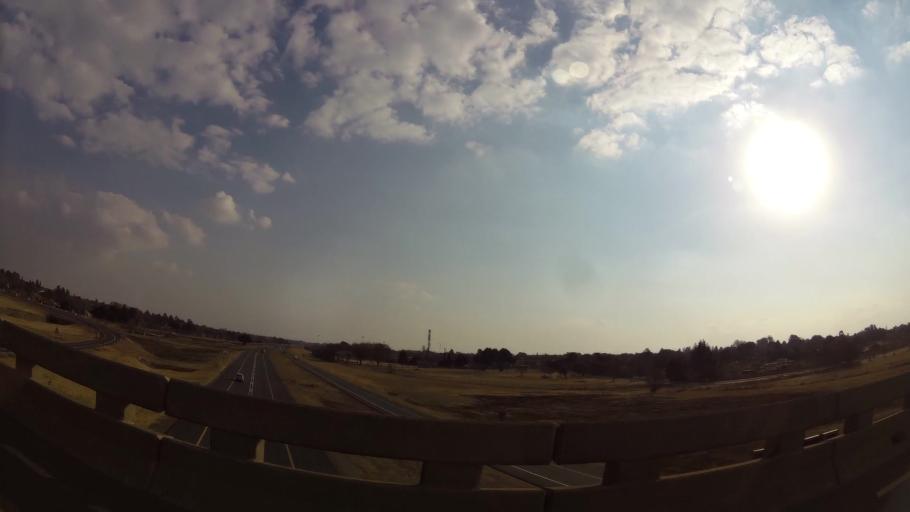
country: ZA
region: Gauteng
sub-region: Ekurhuleni Metropolitan Municipality
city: Springs
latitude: -26.2795
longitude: 28.4529
